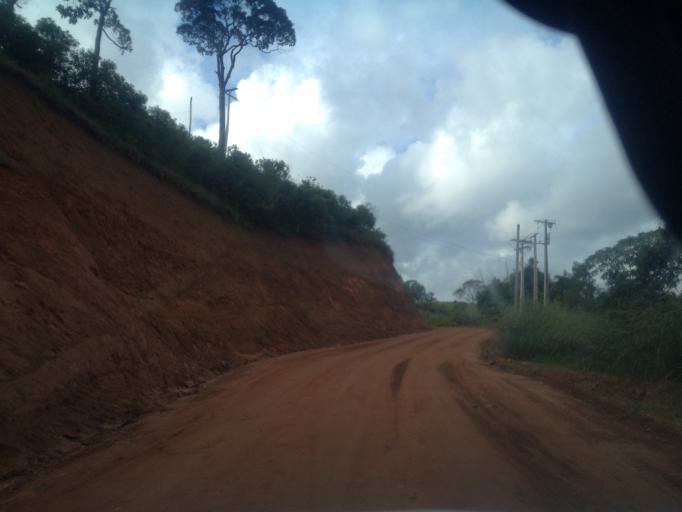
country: BR
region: Rio de Janeiro
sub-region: Quatis
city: Quatis
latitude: -22.2126
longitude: -44.2442
